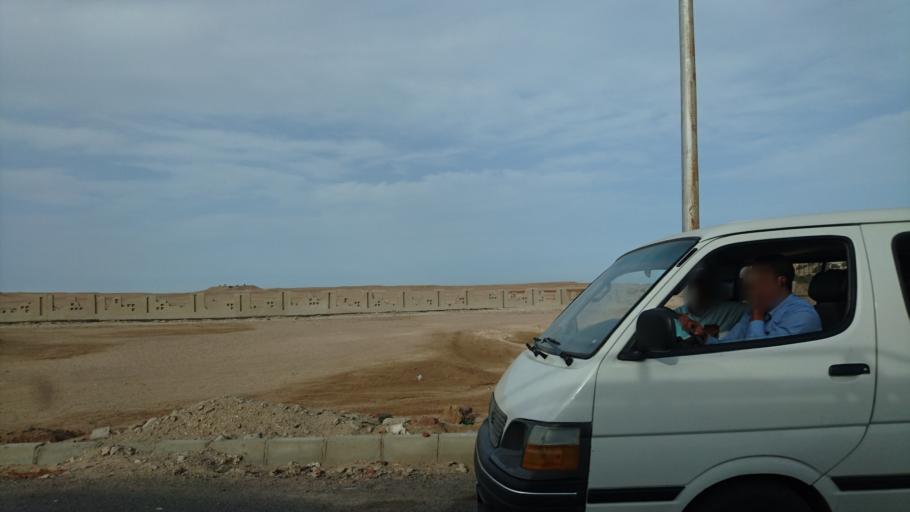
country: EG
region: Red Sea
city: Bur Safajah
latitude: 26.8015
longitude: 33.9384
